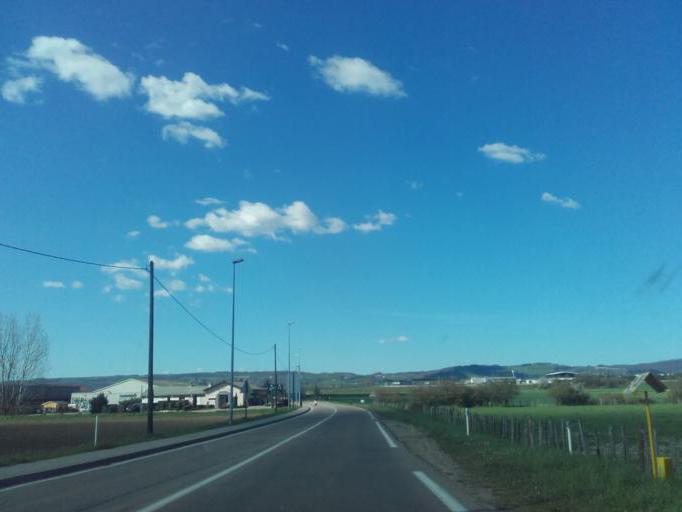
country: FR
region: Rhone-Alpes
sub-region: Departement de l'Isere
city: Saint-Etienne-de-Saint-Geoirs
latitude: 45.3485
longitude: 5.3380
